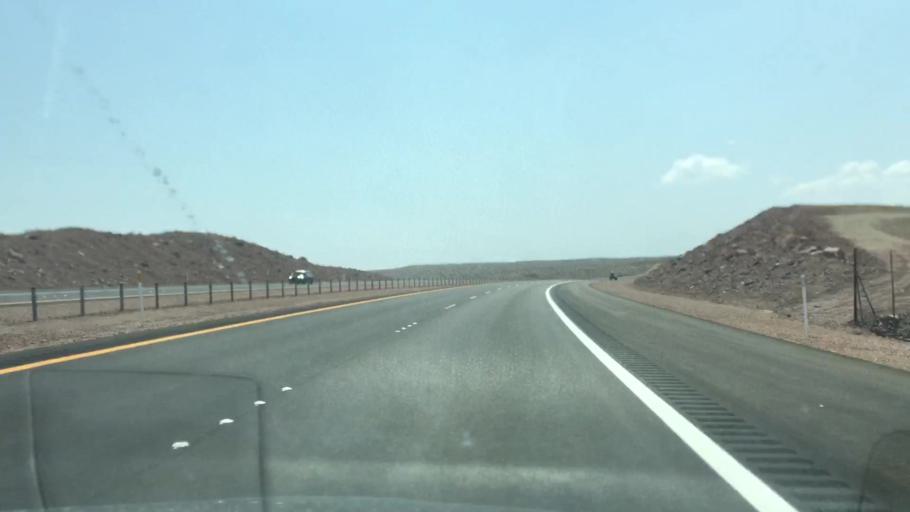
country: US
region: Nevada
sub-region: Clark County
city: Boulder City
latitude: 35.9778
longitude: -114.7924
